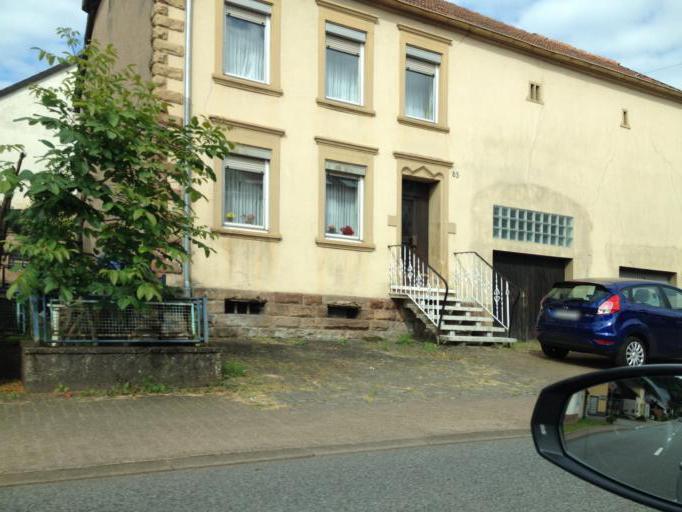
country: DE
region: Saarland
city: Losheim
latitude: 49.4898
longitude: 6.7764
